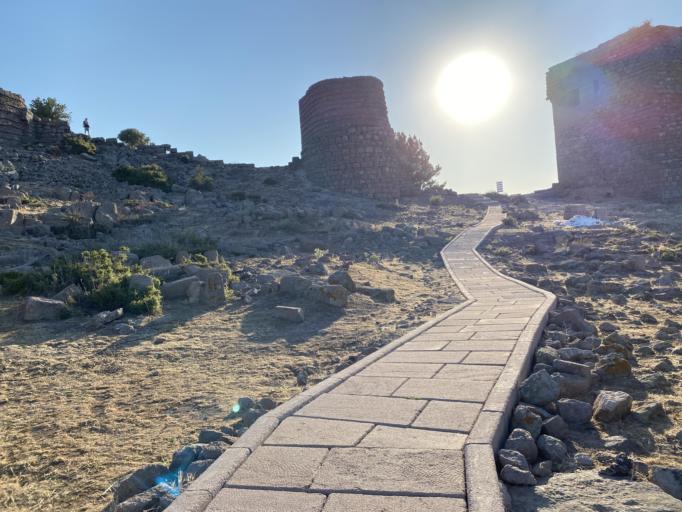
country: TR
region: Canakkale
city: Behram
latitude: 39.4915
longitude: 26.3375
